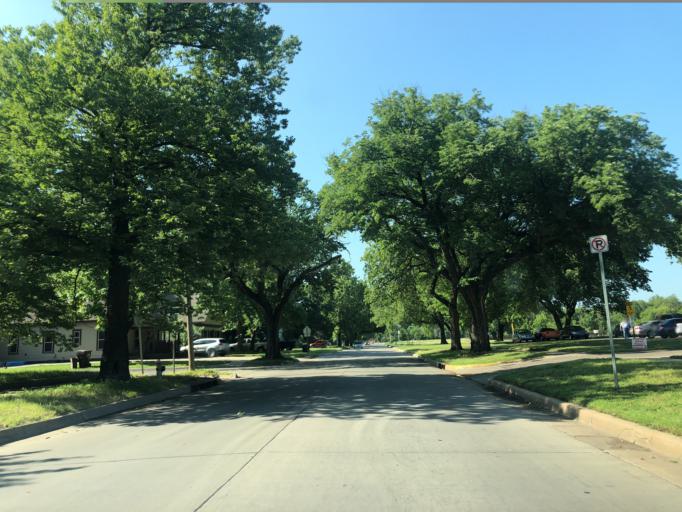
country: US
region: Kansas
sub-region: Sedgwick County
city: Wichita
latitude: 37.7194
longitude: -97.3447
